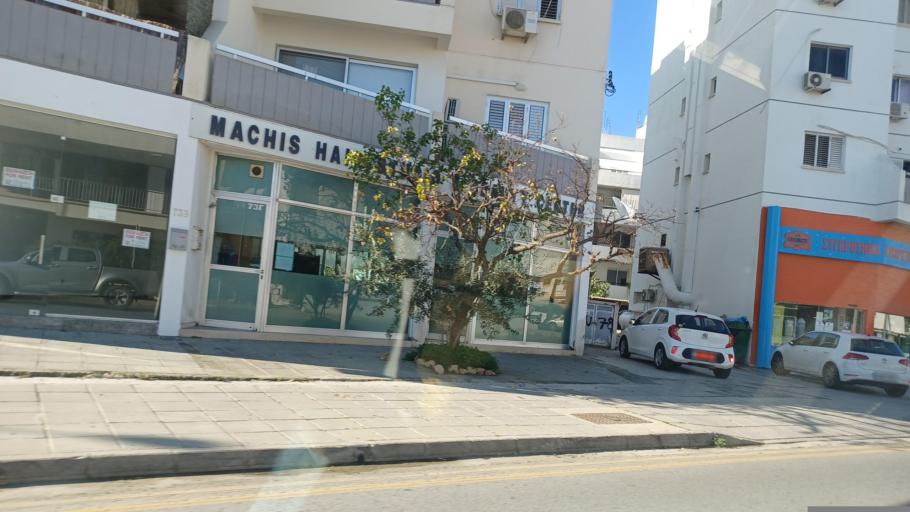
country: CY
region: Lefkosia
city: Nicosia
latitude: 35.1543
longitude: 33.3646
